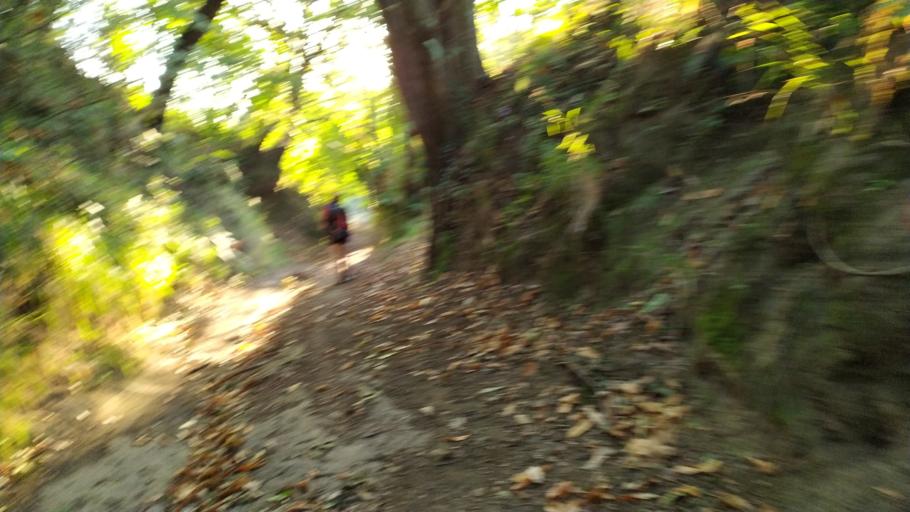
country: IT
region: Campania
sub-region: Provincia di Salerno
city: Lanzara
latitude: 40.7764
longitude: 14.6625
